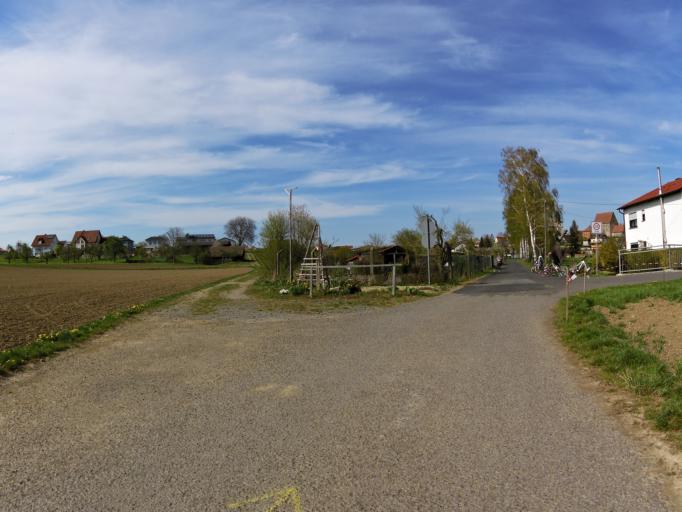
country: DE
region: Bavaria
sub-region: Regierungsbezirk Unterfranken
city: Unterpleichfeld
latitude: 49.8678
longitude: 10.0282
